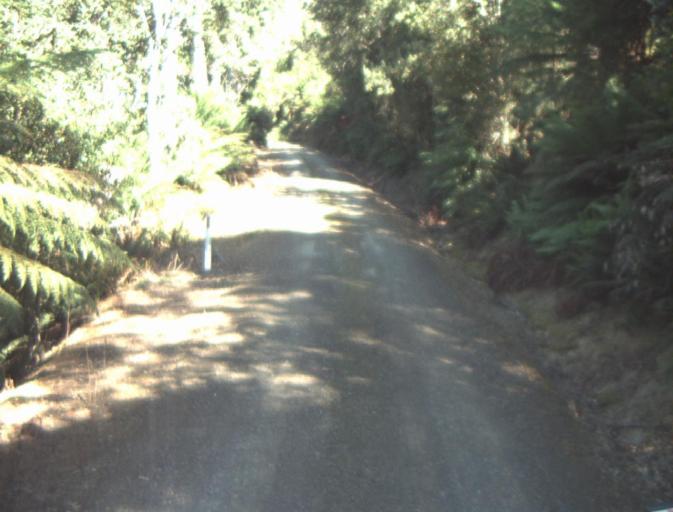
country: AU
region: Tasmania
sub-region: Dorset
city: Scottsdale
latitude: -41.2727
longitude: 147.3651
